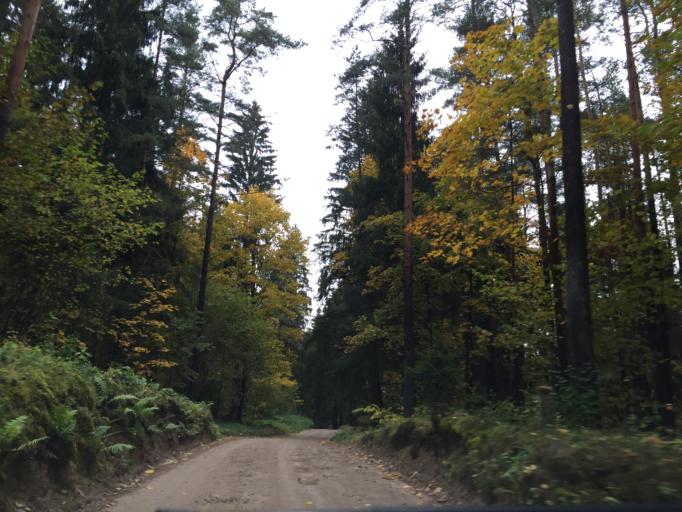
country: LV
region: Ogre
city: Ogre
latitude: 56.8049
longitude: 24.6348
